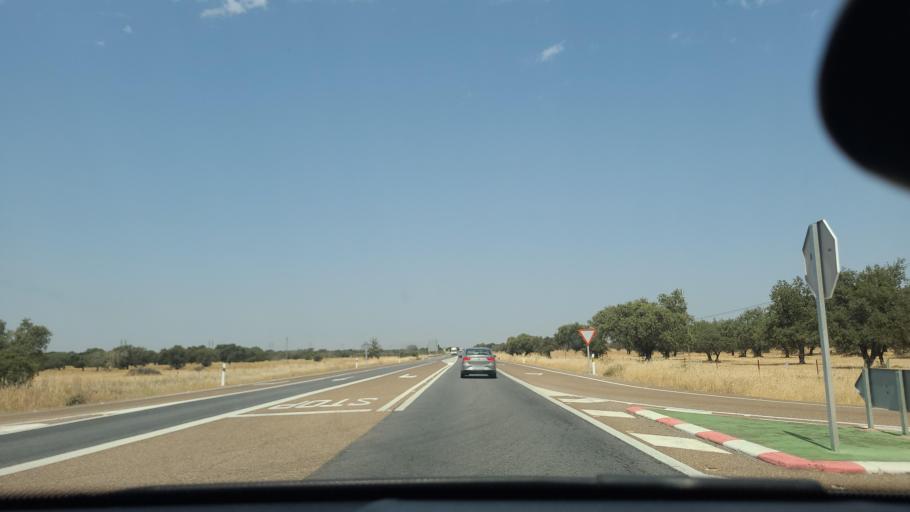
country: ES
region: Extremadura
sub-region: Provincia de Badajoz
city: Entrin Bajo
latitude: 38.6696
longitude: -6.7456
